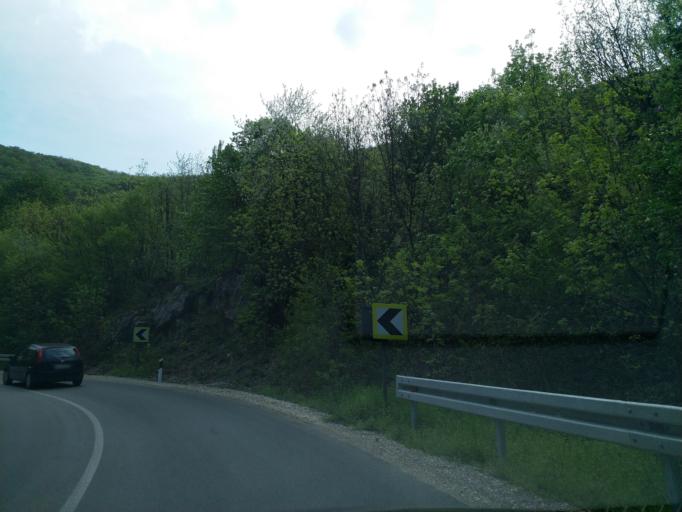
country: RS
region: Central Serbia
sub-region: Pomoravski Okrug
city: Despotovac
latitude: 43.9712
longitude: 21.5245
